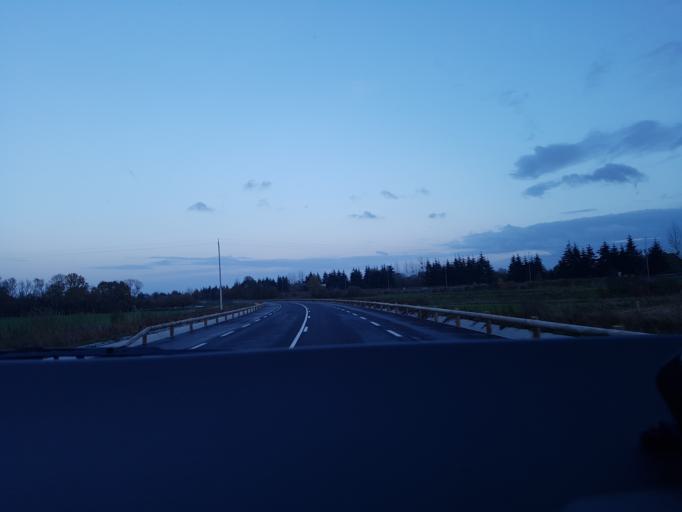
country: FR
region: Haute-Normandie
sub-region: Departement de l'Eure
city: Beuzeville
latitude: 49.3257
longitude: 0.3287
